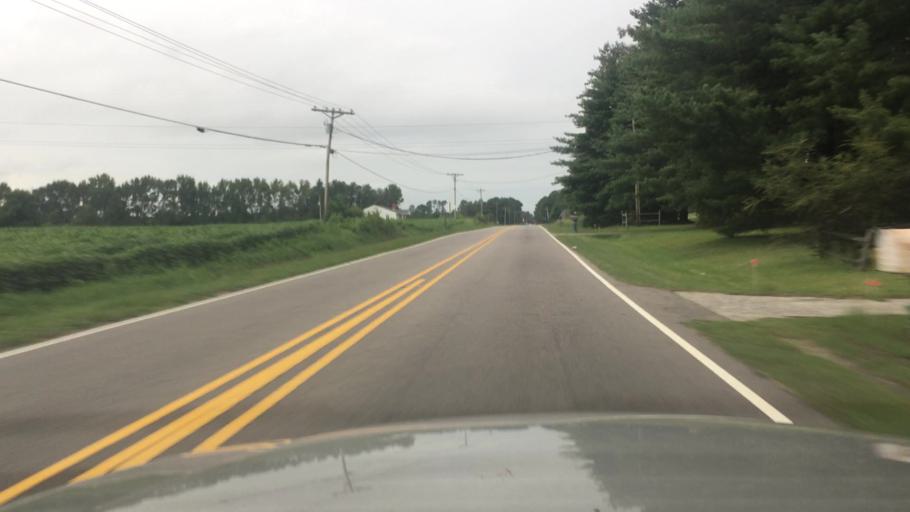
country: US
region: North Carolina
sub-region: Hoke County
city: Rockfish
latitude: 34.9696
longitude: -79.0537
